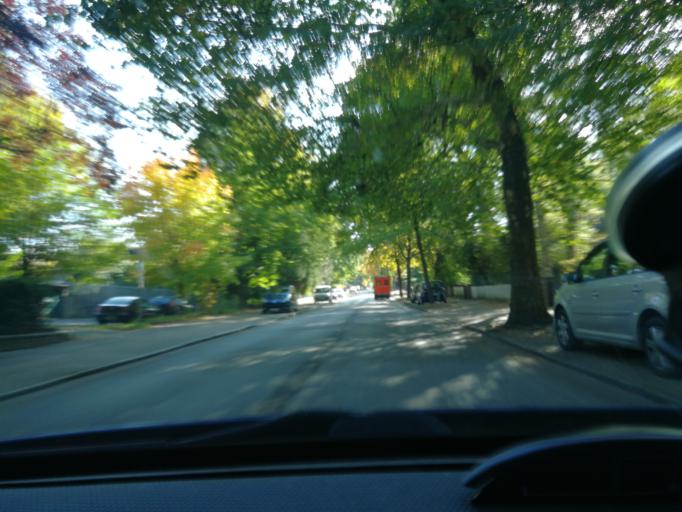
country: DE
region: Hamburg
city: Harburg
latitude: 53.4686
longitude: 9.9468
